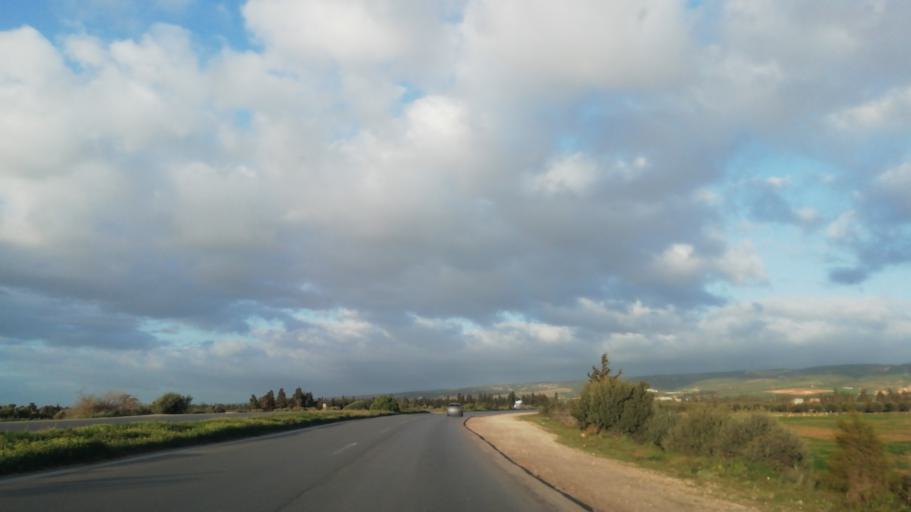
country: DZ
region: Oran
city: Es Senia
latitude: 35.6048
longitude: -0.7354
